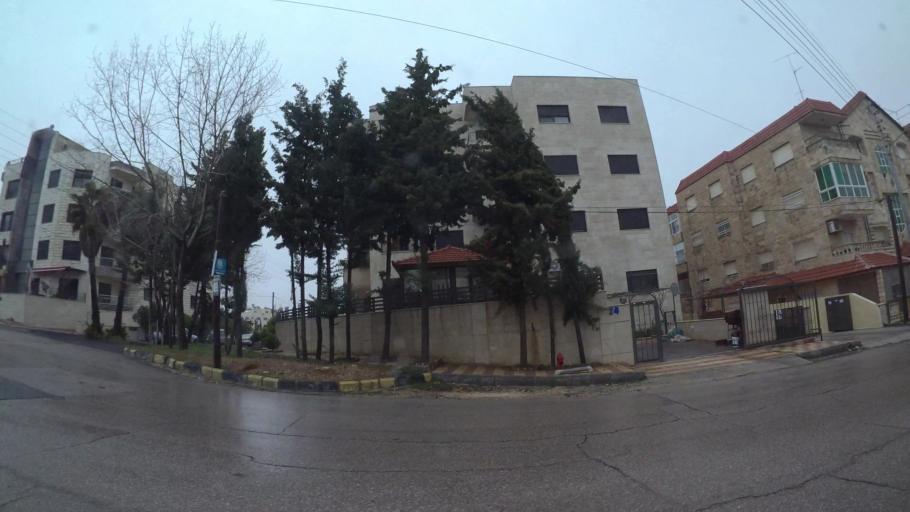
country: JO
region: Amman
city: Al Jubayhah
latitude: 32.0284
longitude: 35.8532
